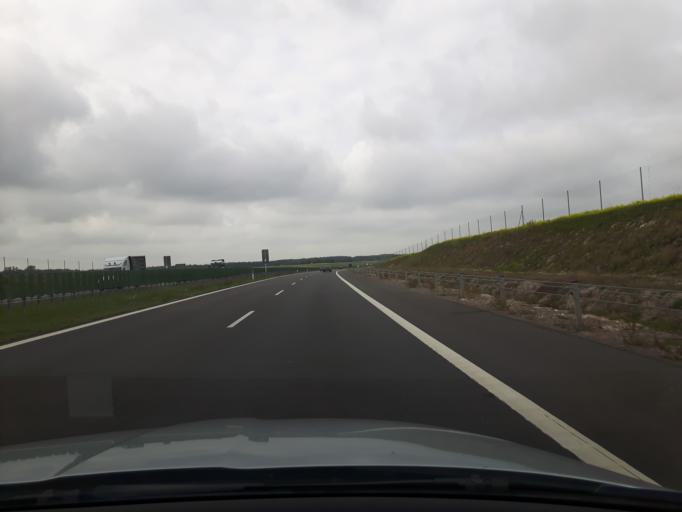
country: PL
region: Swietokrzyskie
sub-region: Powiat jedrzejowski
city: Sobkow
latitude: 50.6974
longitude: 20.3924
